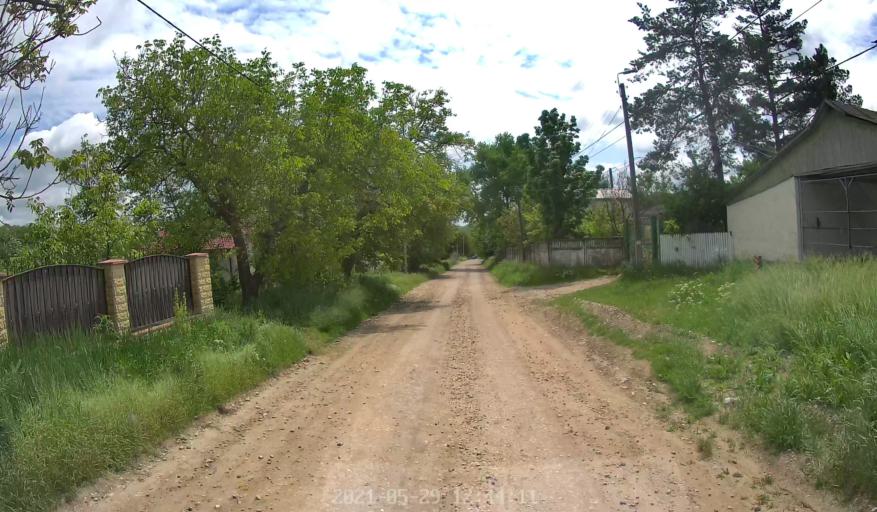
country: MD
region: Hincesti
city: Hincesti
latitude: 46.8713
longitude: 28.6386
